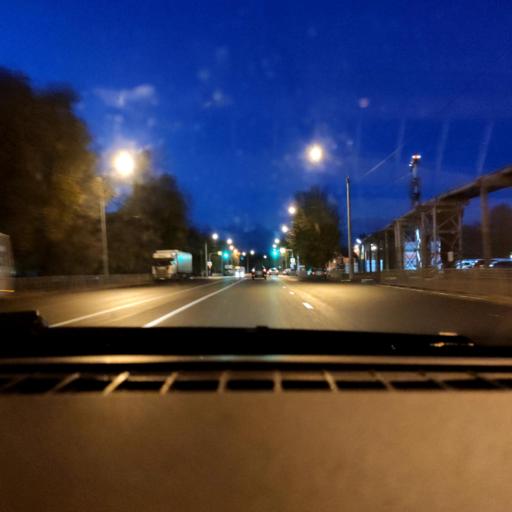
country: RU
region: Voronezj
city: Maslovka
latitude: 51.6028
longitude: 39.2437
